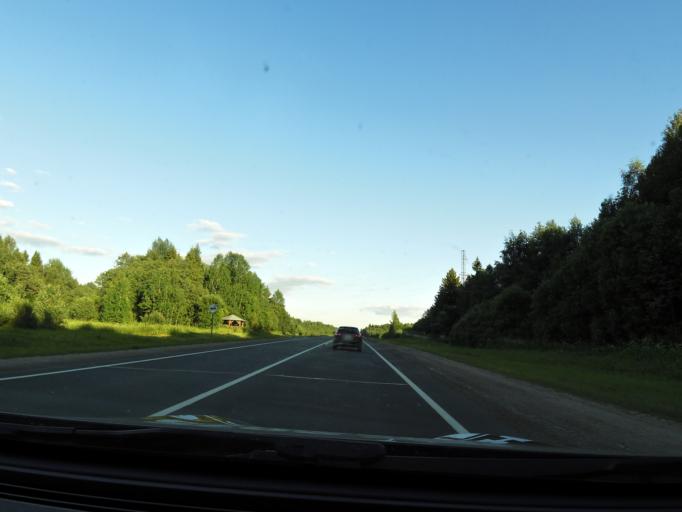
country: RU
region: Vologda
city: Vologda
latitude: 59.1324
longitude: 39.9572
